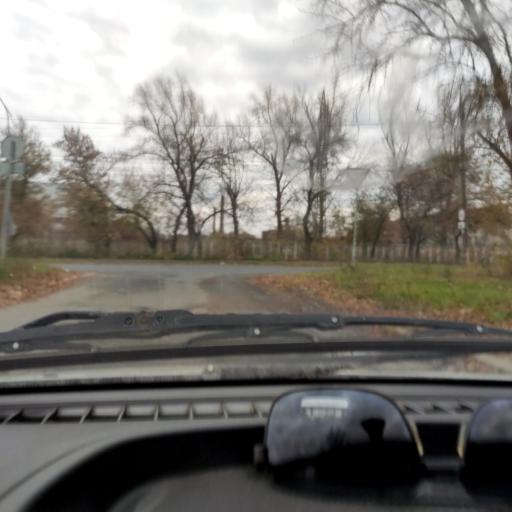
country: RU
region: Samara
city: Tol'yatti
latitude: 53.5287
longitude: 49.4363
